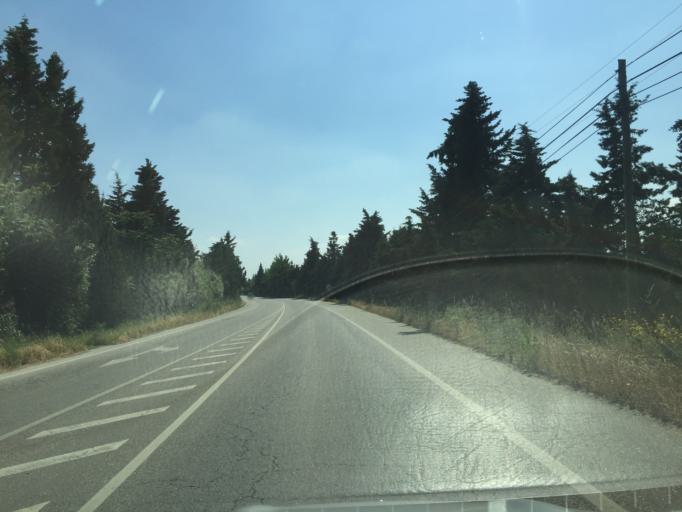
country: PT
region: Santarem
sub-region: Golega
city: Golega
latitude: 39.3859
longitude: -8.4485
